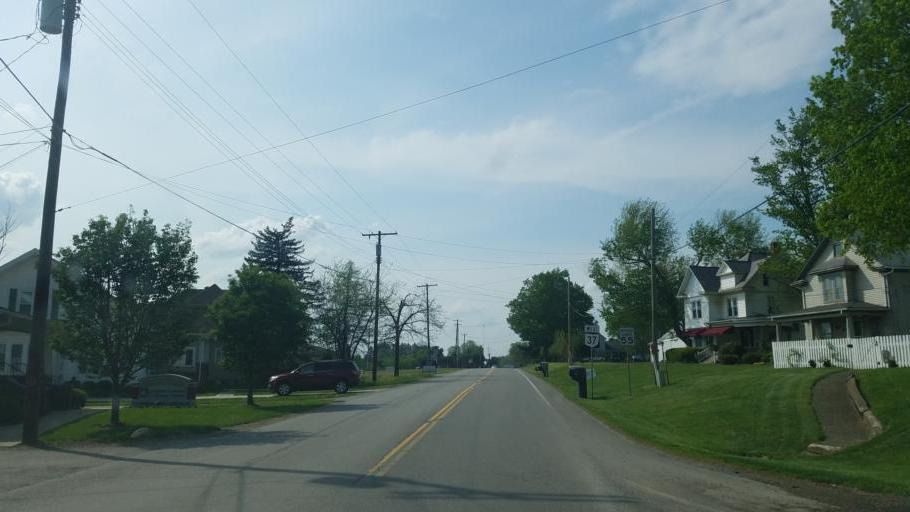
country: US
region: Ohio
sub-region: Licking County
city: Beechwood Trails
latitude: 40.0921
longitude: -82.6178
